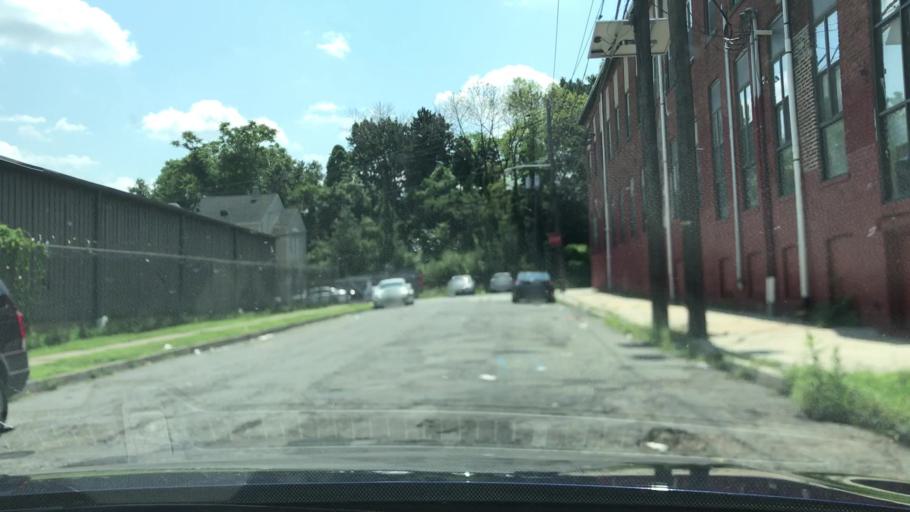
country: US
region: New Jersey
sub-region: Passaic County
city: Paterson
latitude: 40.9088
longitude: -74.1701
